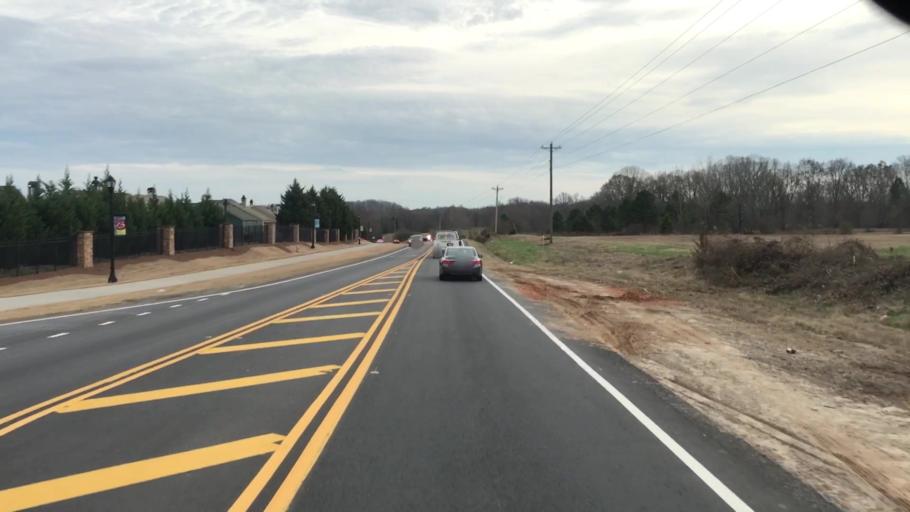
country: US
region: Georgia
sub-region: Jackson County
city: Braselton
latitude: 34.1187
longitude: -83.8254
